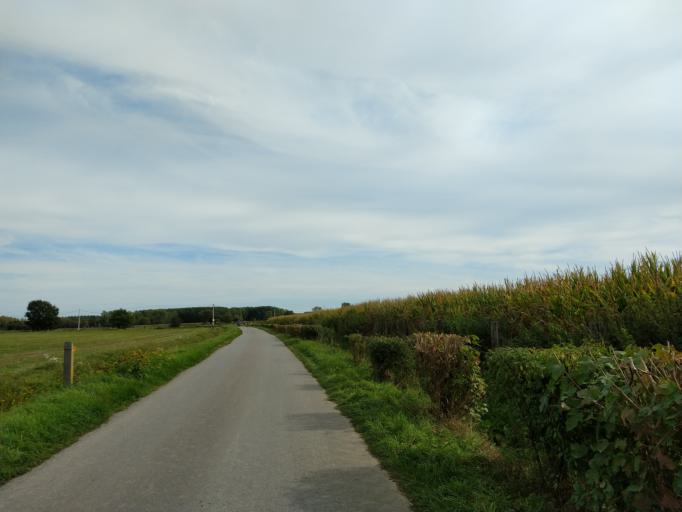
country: BE
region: Flanders
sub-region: Provincie Vlaams-Brabant
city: Haacht
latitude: 50.9660
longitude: 4.6683
